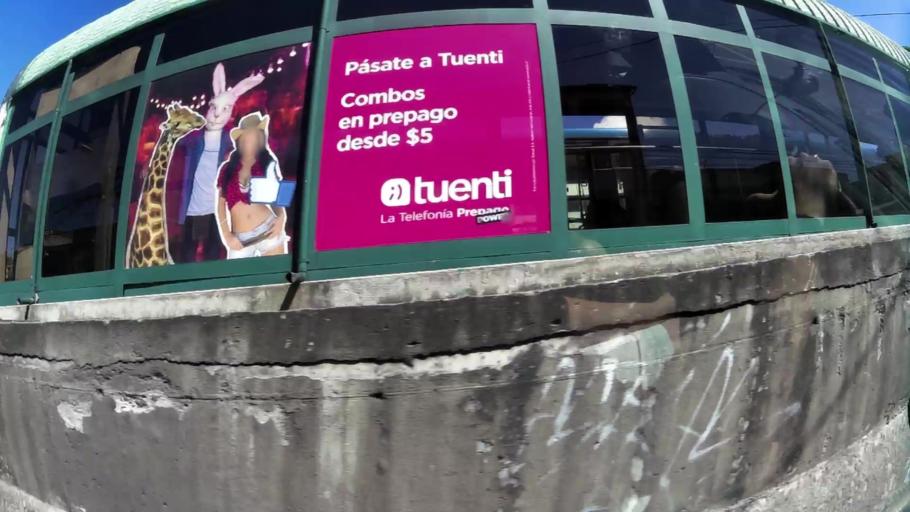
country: EC
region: Pichincha
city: Quito
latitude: -0.1831
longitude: -78.4950
